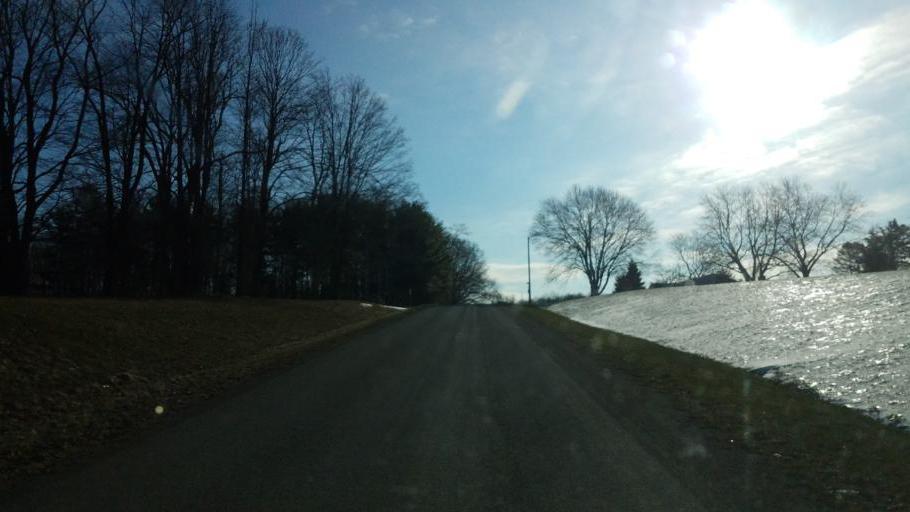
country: US
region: Ohio
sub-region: Sandusky County
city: Bellville
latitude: 40.6092
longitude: -82.5446
